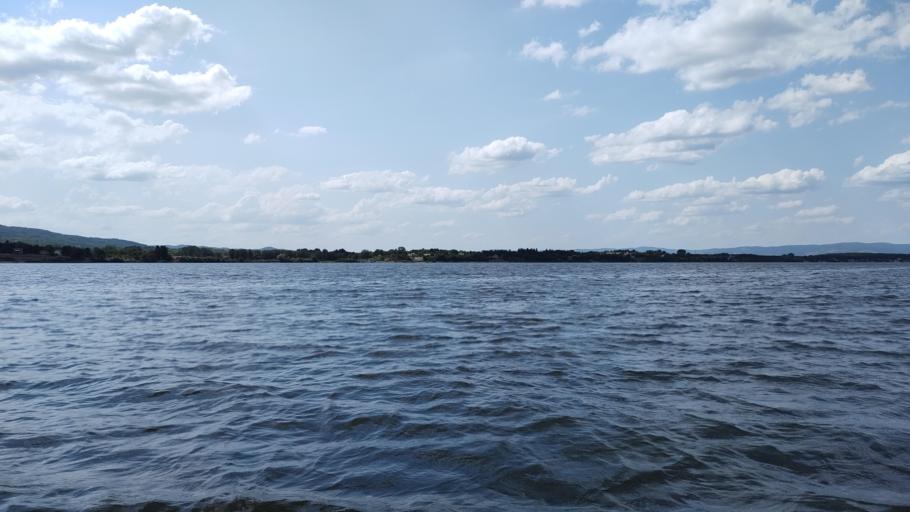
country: RS
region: Central Serbia
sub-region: Branicevski Okrug
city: Golubac
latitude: 44.6802
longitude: 21.6168
